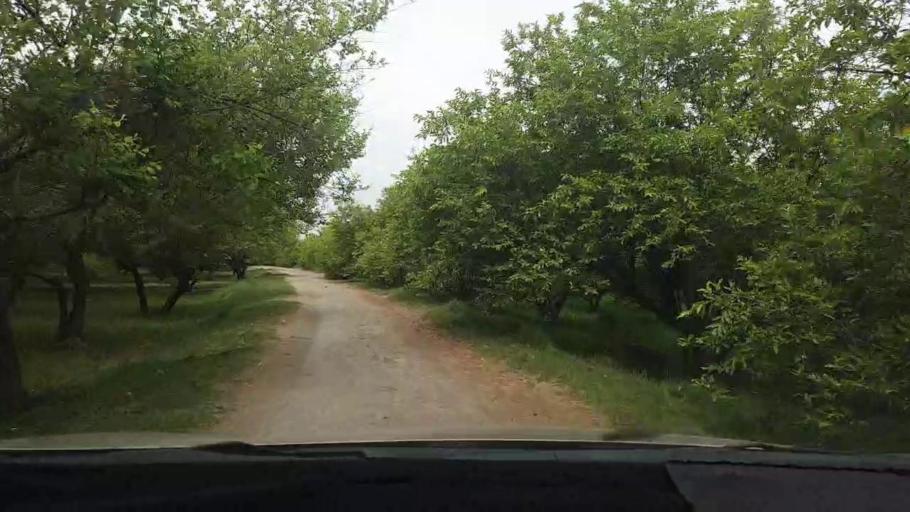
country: PK
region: Sindh
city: Naudero
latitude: 27.6349
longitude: 68.3412
